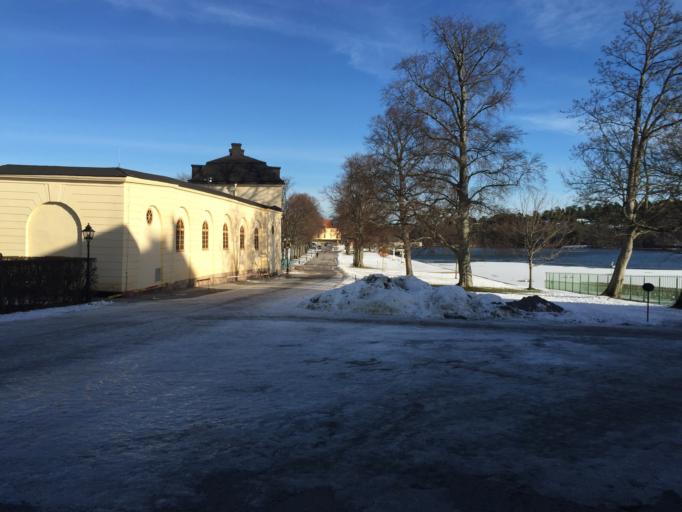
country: SE
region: Stockholm
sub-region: Stockholms Kommun
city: Bromma
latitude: 59.3224
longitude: 17.8865
